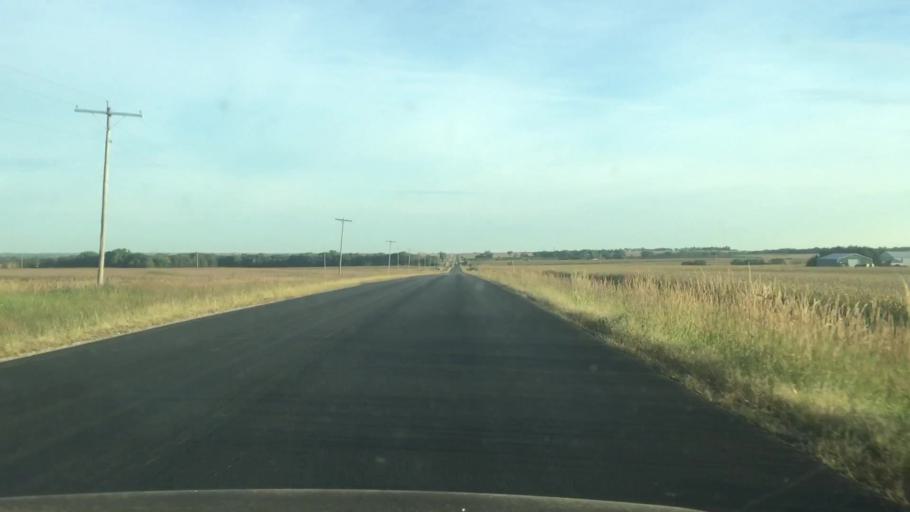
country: US
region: Kansas
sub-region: Marshall County
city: Marysville
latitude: 39.8675
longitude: -96.6009
